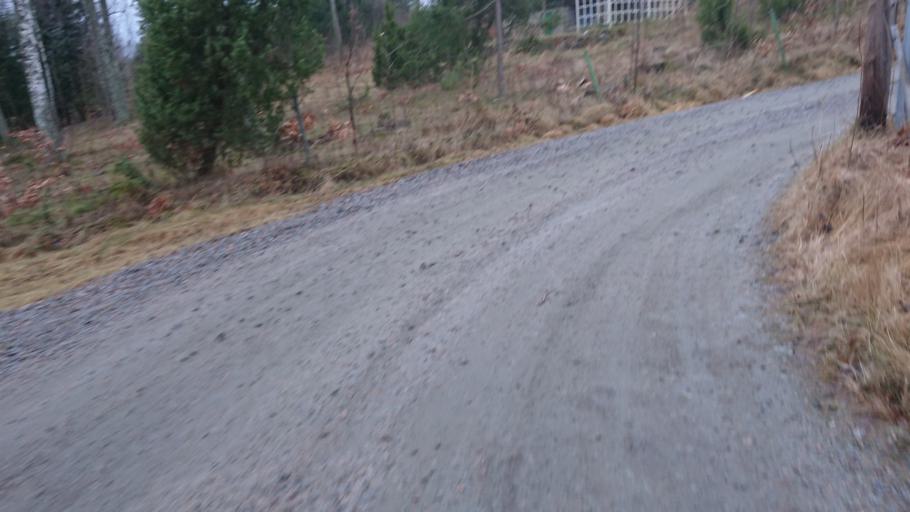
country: SE
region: Uppsala
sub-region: Osthammars Kommun
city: Bjorklinge
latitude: 60.0249
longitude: 17.5775
